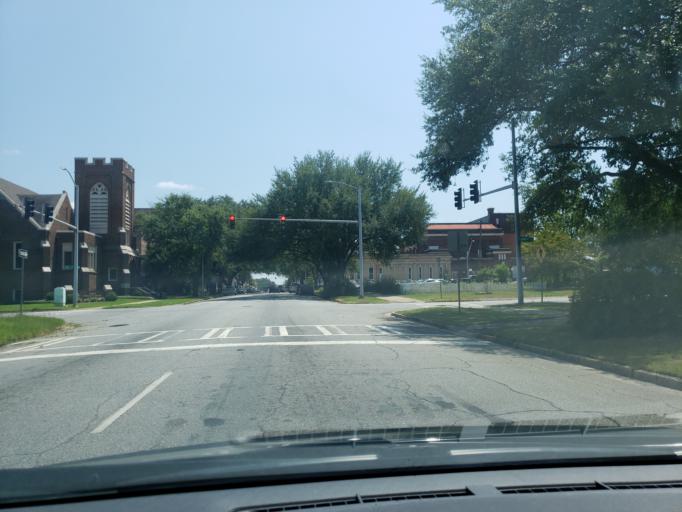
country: US
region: Georgia
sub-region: Dougherty County
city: Albany
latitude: 31.5803
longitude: -84.1537
